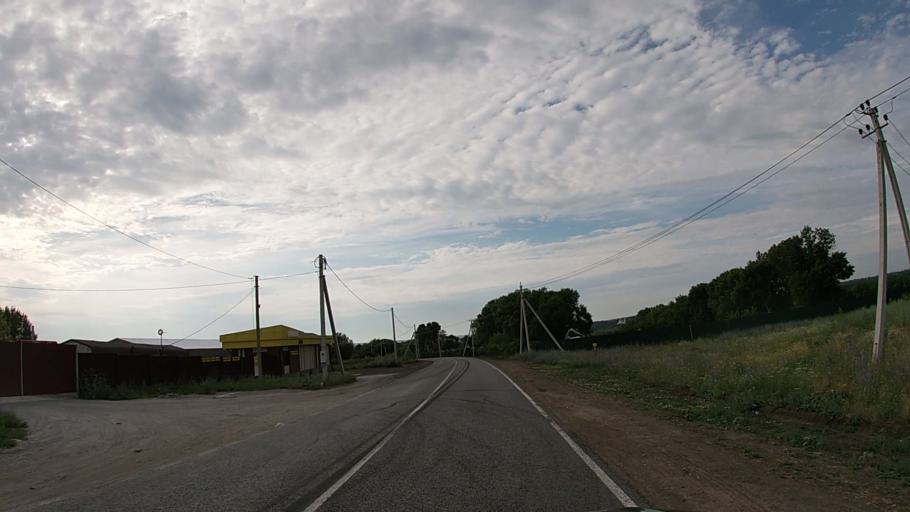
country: RU
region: Belgorod
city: Severnyy
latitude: 50.7198
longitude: 36.5858
